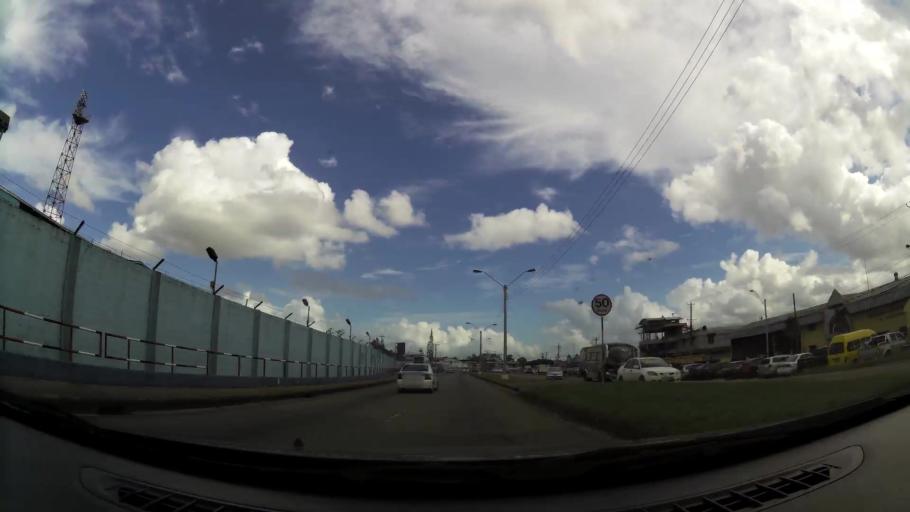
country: TT
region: City of San Fernando
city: San Fernando
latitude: 10.2658
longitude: -61.4606
